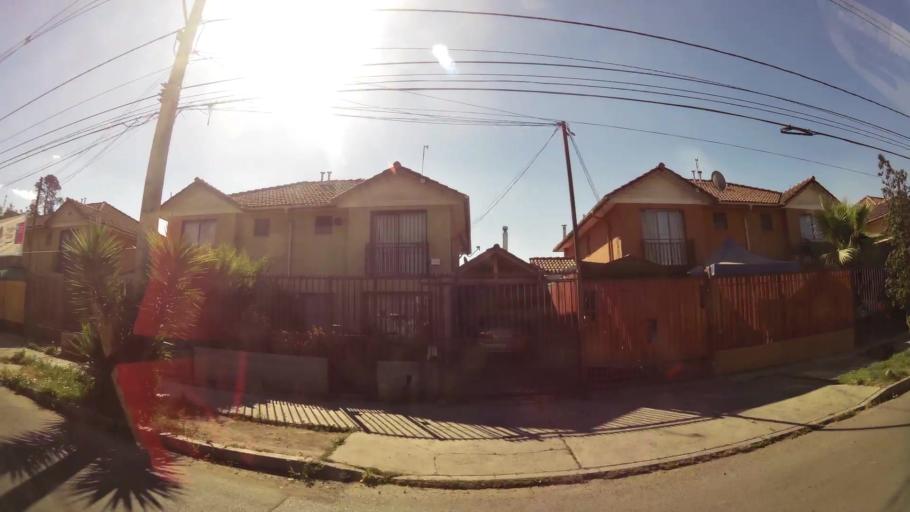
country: CL
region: Santiago Metropolitan
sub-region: Provincia de Maipo
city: San Bernardo
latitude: -33.5537
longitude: -70.7685
